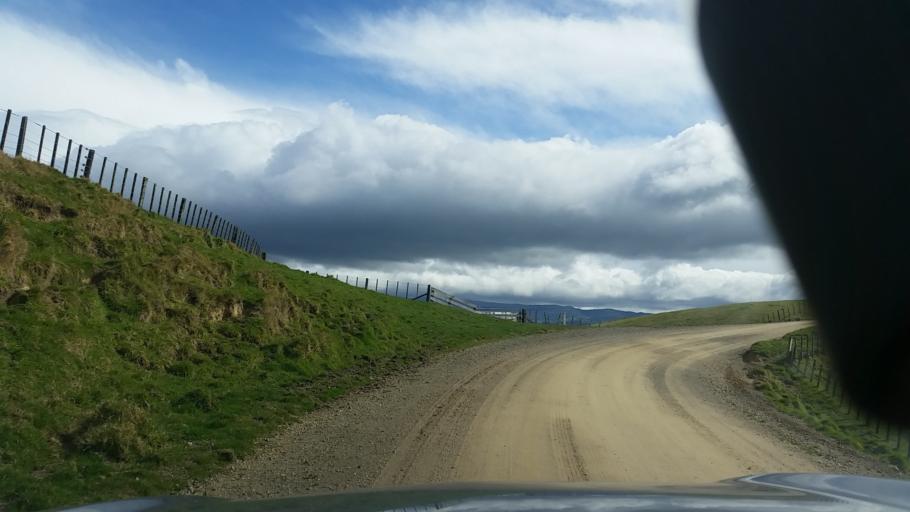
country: NZ
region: Hawke's Bay
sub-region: Napier City
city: Napier
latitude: -39.2035
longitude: 176.9522
